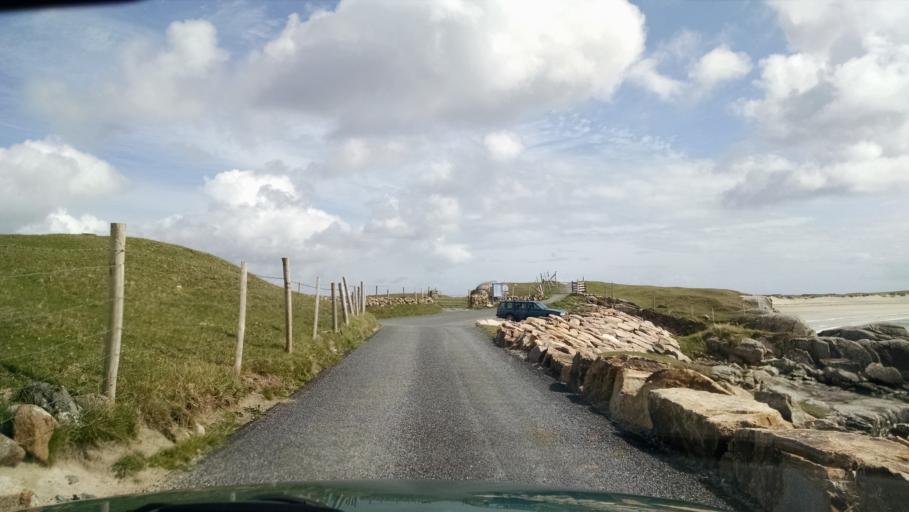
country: IE
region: Connaught
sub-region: County Galway
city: Clifden
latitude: 53.3814
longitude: -9.9637
